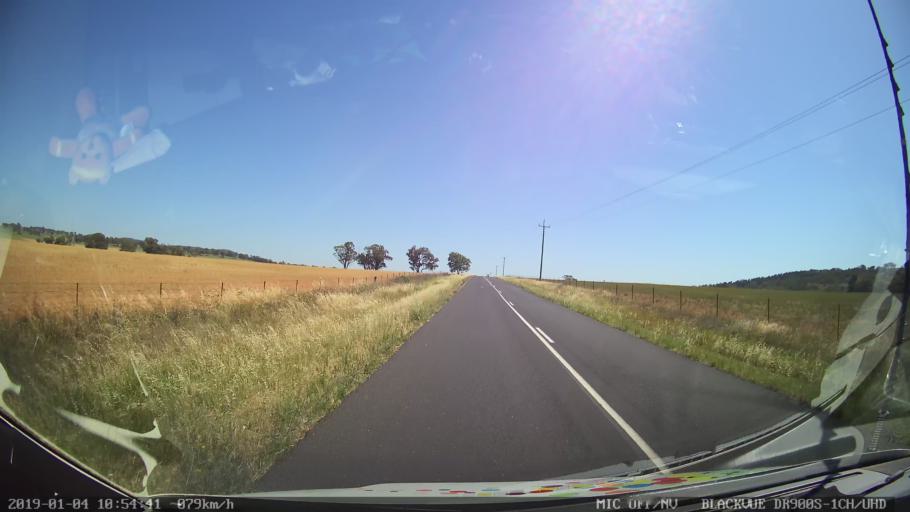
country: AU
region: New South Wales
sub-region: Cabonne
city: Molong
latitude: -33.2022
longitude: 148.6905
